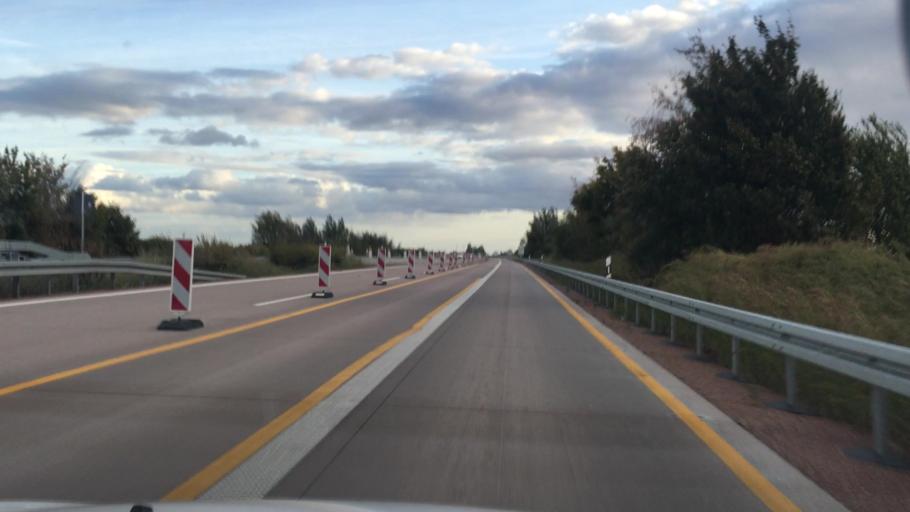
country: DE
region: Saxony-Anhalt
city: Nauendorf
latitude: 51.6069
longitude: 11.8702
